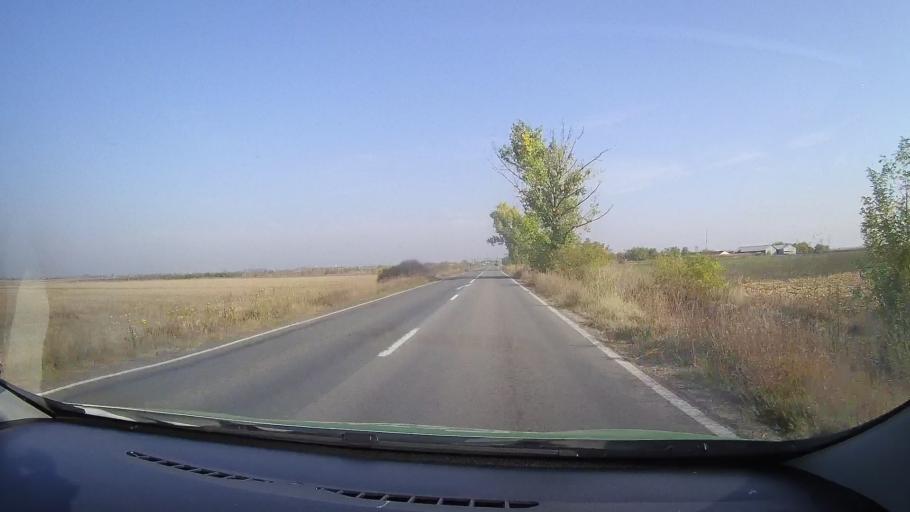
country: RO
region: Arad
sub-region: Comuna Pilu
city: Pilu
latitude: 46.6021
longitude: 21.3502
